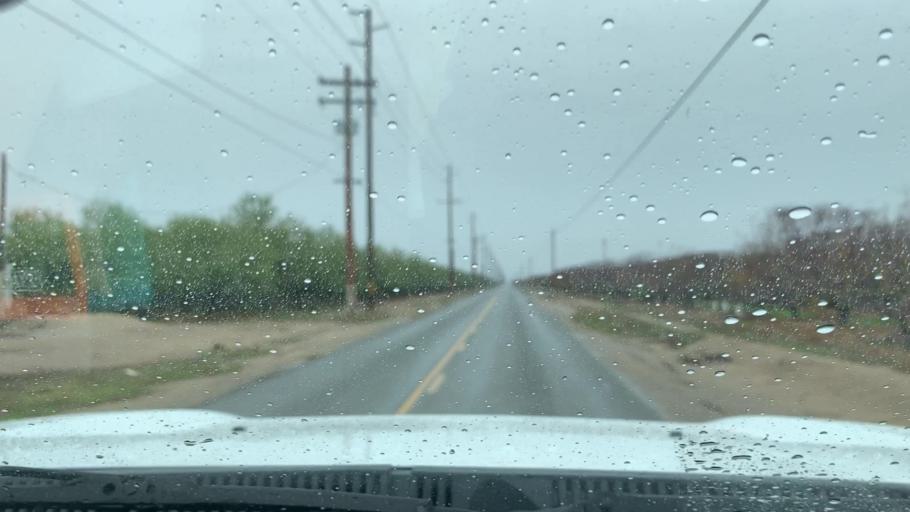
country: US
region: California
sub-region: Kern County
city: Delano
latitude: 35.8341
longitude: -119.2051
